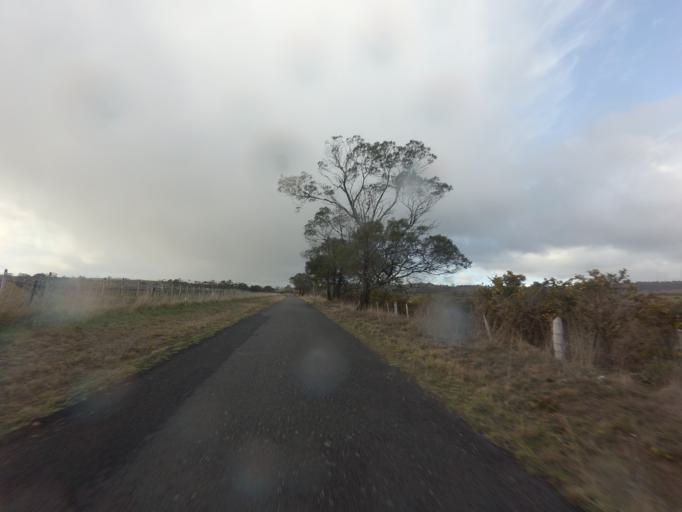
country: AU
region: Tasmania
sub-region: Break O'Day
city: St Helens
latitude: -42.0019
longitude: 148.0865
